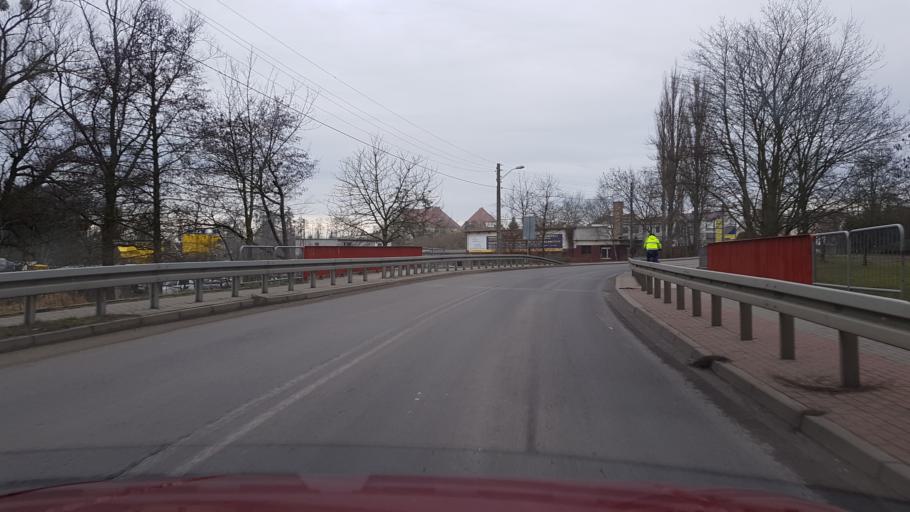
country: PL
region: West Pomeranian Voivodeship
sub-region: Powiat policki
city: Police
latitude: 53.5910
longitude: 14.5428
